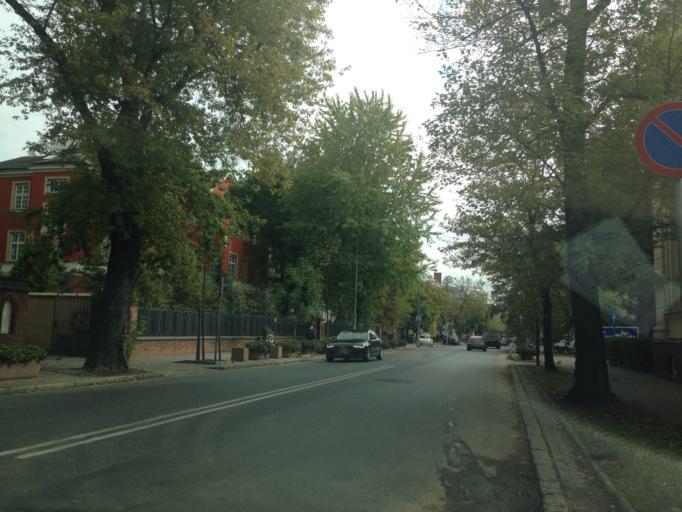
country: PL
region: Masovian Voivodeship
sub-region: Warszawa
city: Praga Polnoc
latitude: 52.2514
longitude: 21.0303
